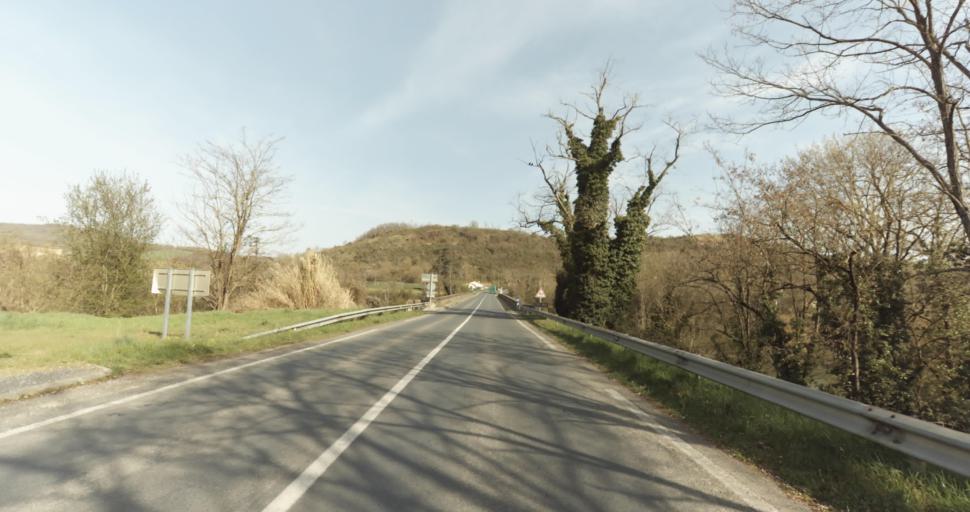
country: FR
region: Midi-Pyrenees
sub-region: Departement du Tarn
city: Saint-Sulpice-la-Pointe
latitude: 43.7840
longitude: 1.6790
